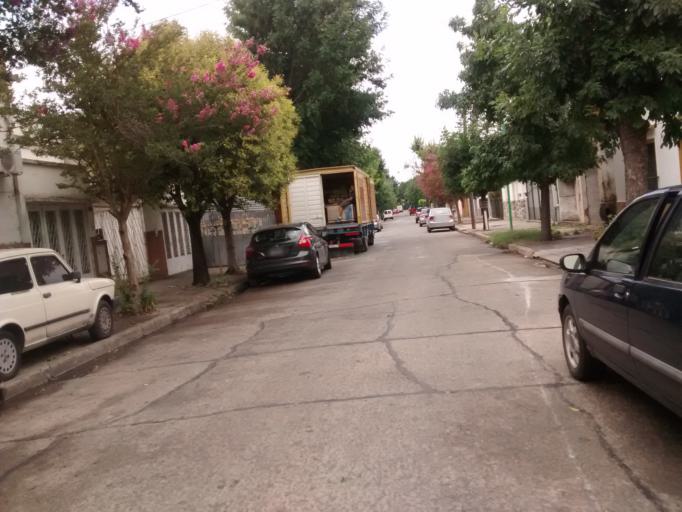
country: AR
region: Buenos Aires
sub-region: Partido de La Plata
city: La Plata
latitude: -34.8940
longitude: -57.9690
